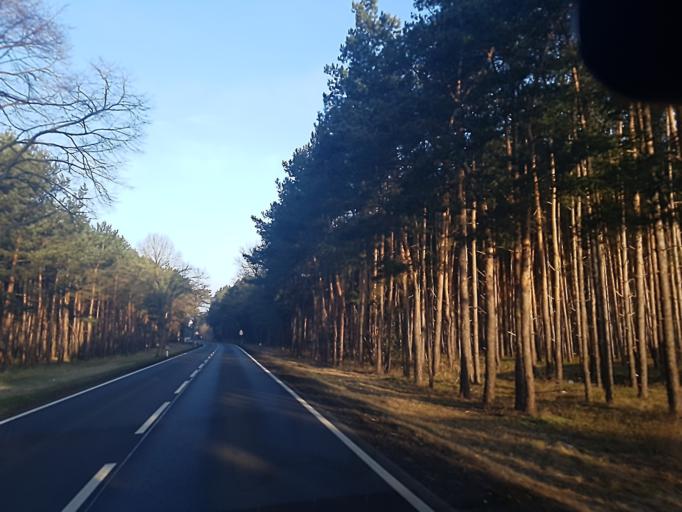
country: DE
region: Brandenburg
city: Linthe
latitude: 52.1605
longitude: 12.7789
